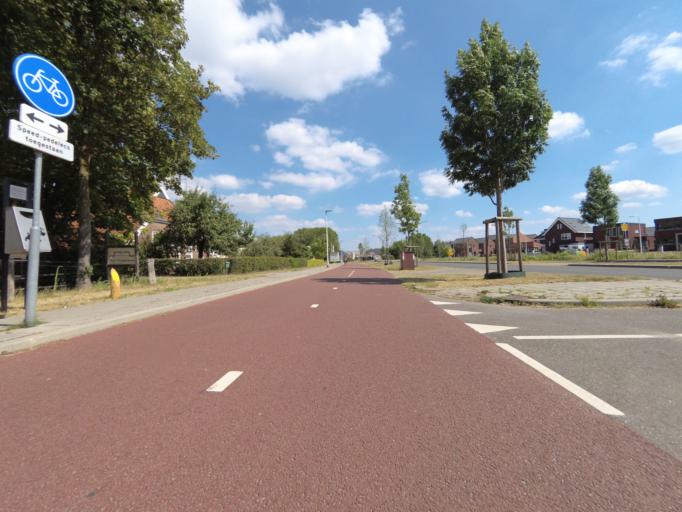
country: NL
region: Overijssel
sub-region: Gemeente Almelo
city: Almelo
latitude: 52.3645
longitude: 6.6553
